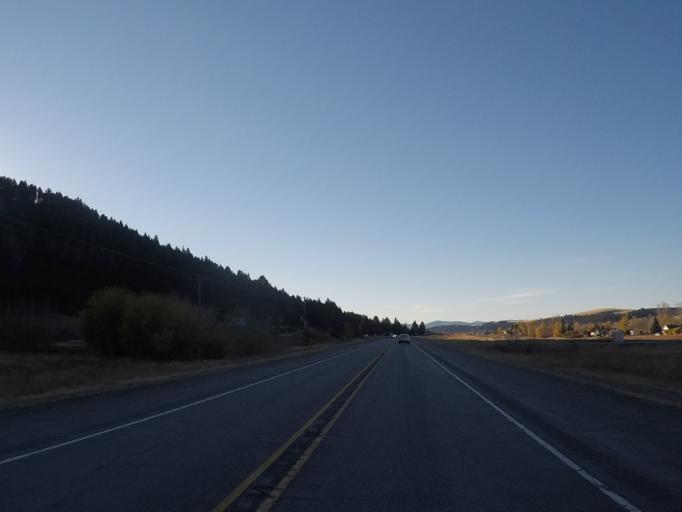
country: US
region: Montana
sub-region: Lewis and Clark County
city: Helena West Side
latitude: 46.5580
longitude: -112.4199
